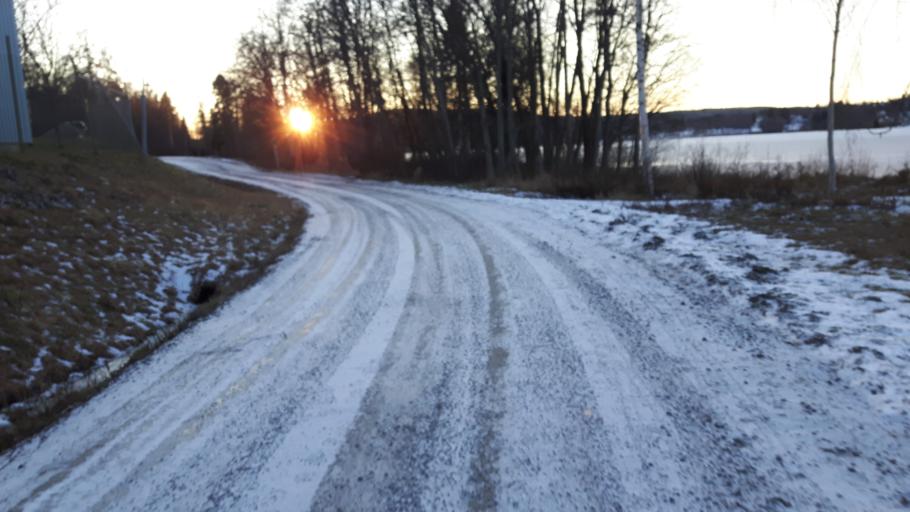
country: SE
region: Vaesternorrland
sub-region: Haernoesands Kommun
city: Haernoesand
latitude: 62.6212
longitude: 17.9365
